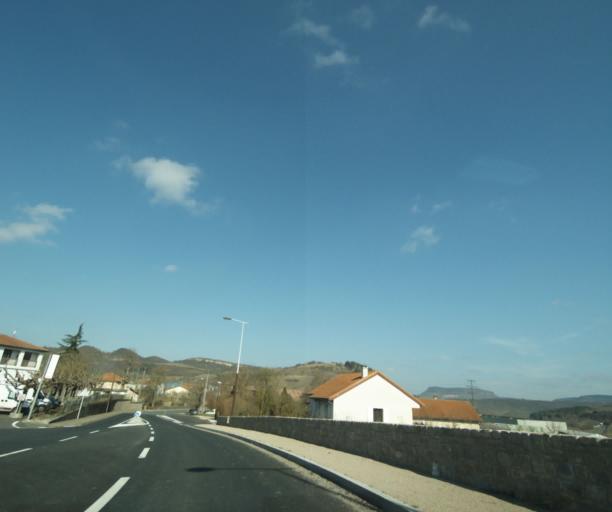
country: FR
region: Midi-Pyrenees
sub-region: Departement de l'Aveyron
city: Saint-Affrique
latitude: 43.9725
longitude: 2.9617
